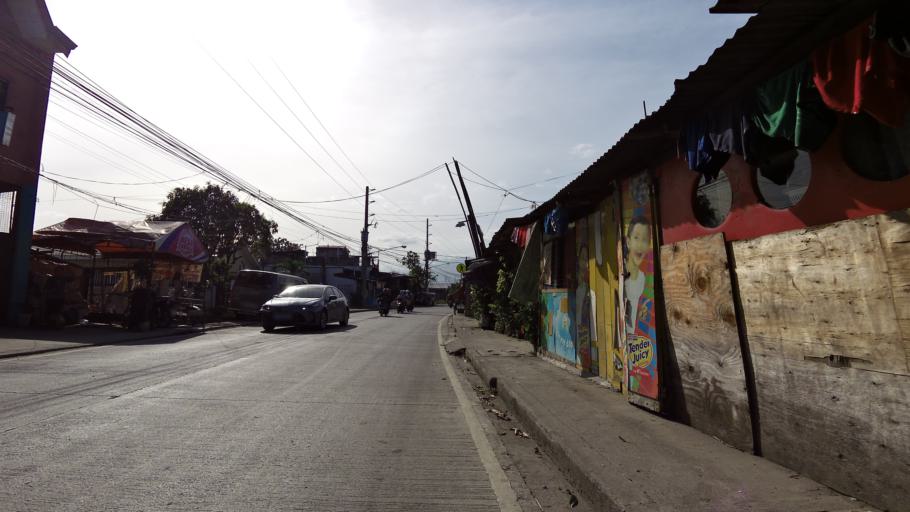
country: PH
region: Calabarzon
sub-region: Province of Rizal
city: Taytay
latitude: 14.5421
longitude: 121.1126
